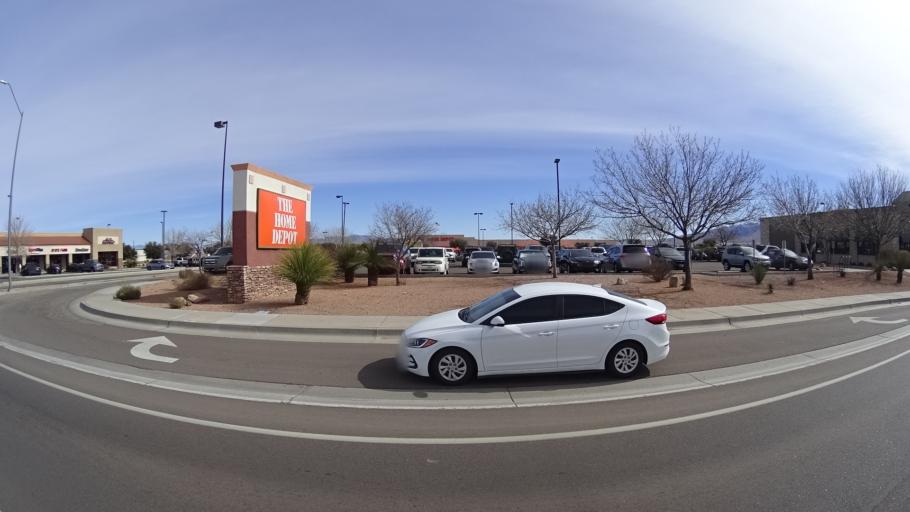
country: US
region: Arizona
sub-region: Mohave County
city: New Kingman-Butler
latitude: 35.2348
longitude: -114.0373
